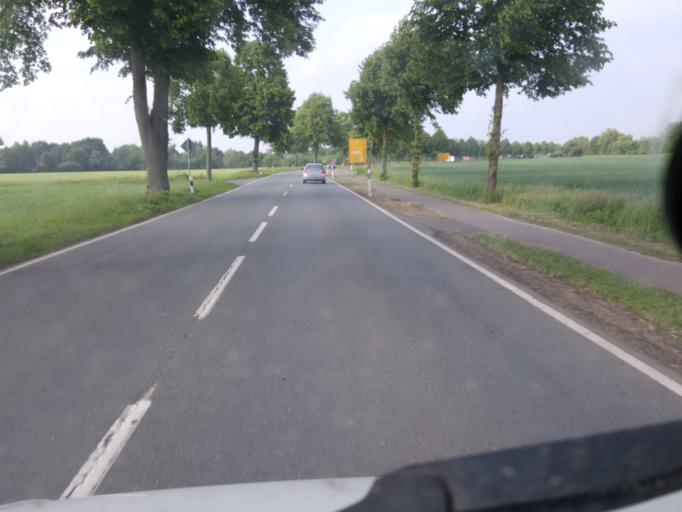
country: DE
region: Lower Saxony
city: Marklohe
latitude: 52.6488
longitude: 9.1478
